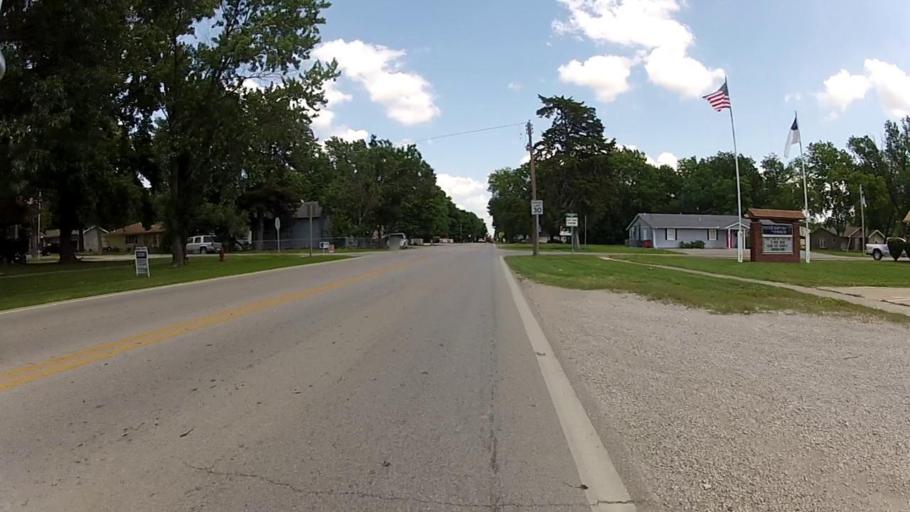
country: US
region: Kansas
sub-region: Labette County
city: Altamont
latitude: 37.1930
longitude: -95.2944
